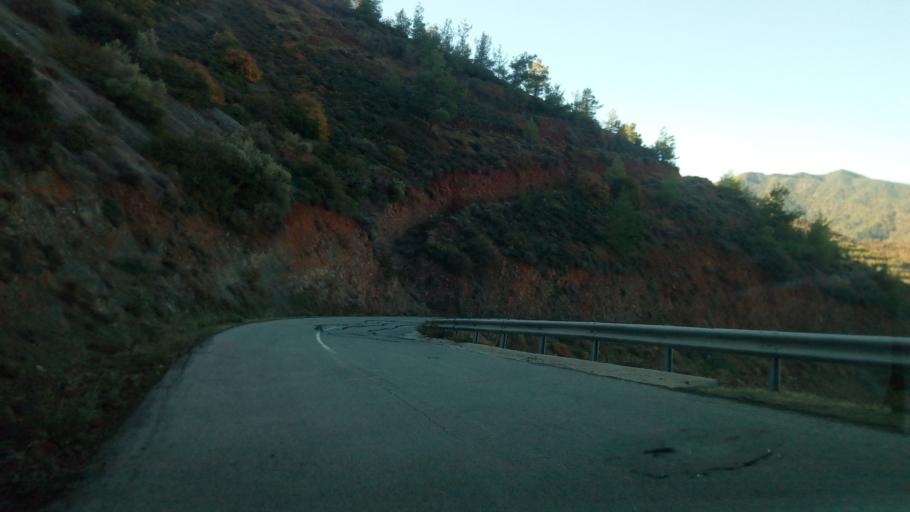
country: CY
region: Lefkosia
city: Lefka
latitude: 35.0734
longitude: 32.8199
